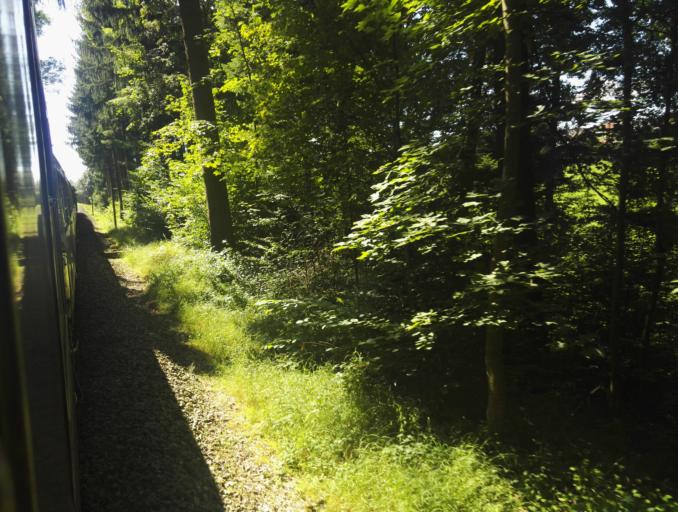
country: DE
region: Baden-Wuerttemberg
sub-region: Regierungsbezirk Stuttgart
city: Welzheim
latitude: 48.8622
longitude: 9.6266
